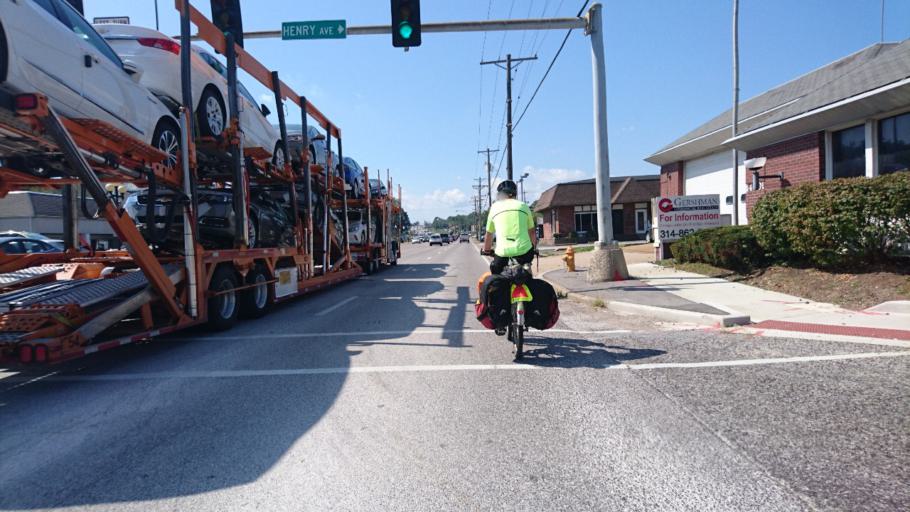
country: US
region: Missouri
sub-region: Saint Louis County
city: Manchester
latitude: 38.5932
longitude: -90.5161
